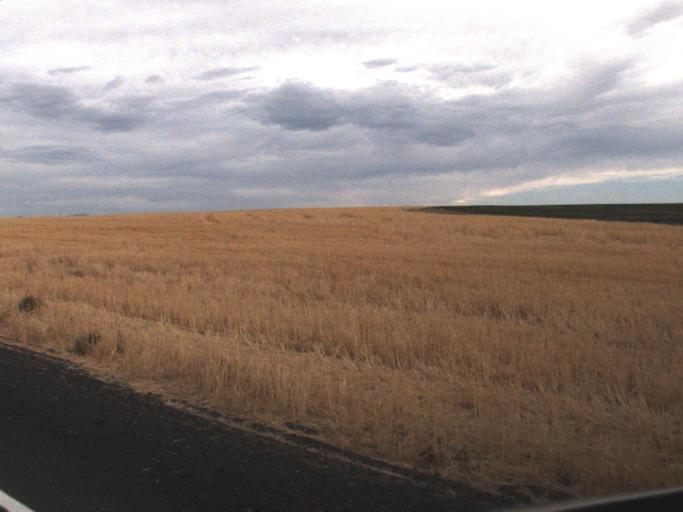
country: US
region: Washington
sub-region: Okanogan County
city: Coulee Dam
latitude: 47.6321
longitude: -118.7208
